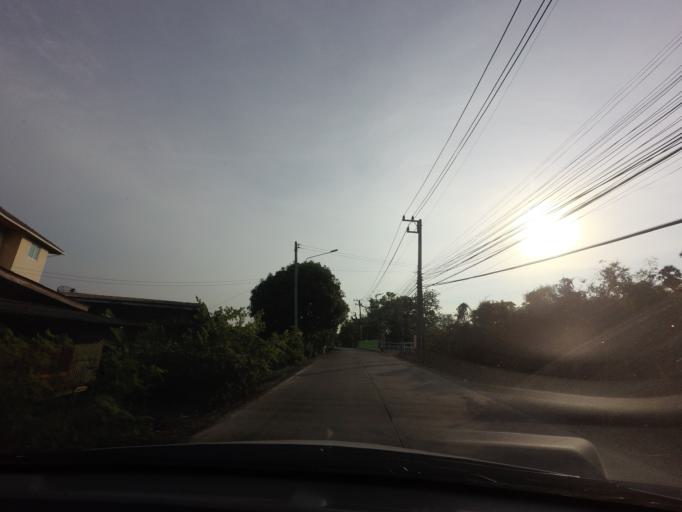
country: TH
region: Pathum Thani
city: Pathum Thani
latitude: 14.0389
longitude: 100.5488
